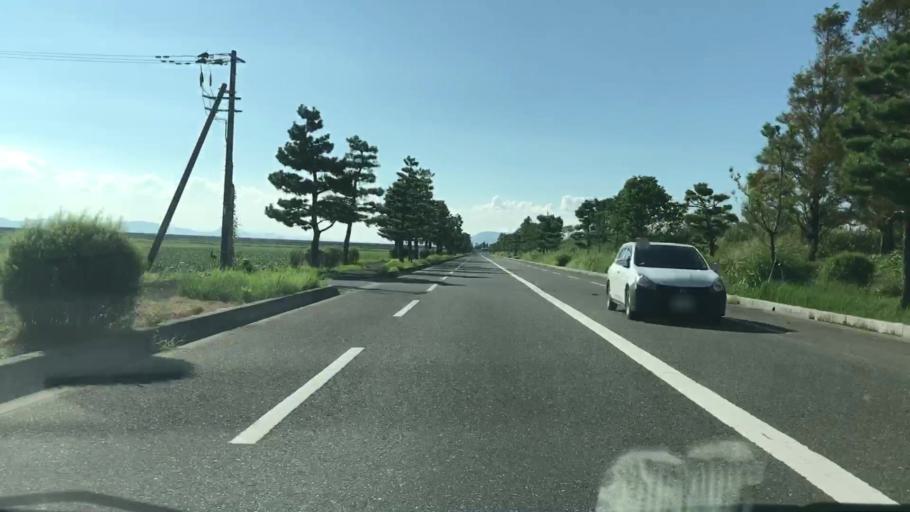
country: JP
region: Saga Prefecture
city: Okawa
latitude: 33.1573
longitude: 130.2968
